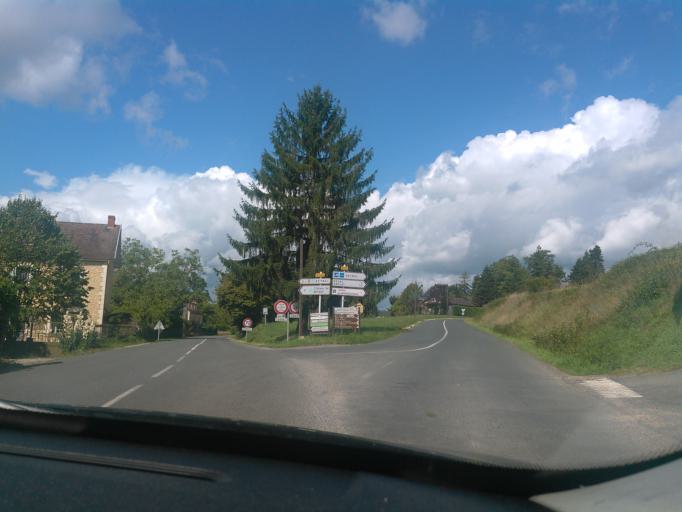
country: FR
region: Aquitaine
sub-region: Departement de la Dordogne
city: Cenac-et-Saint-Julien
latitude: 44.8235
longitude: 1.1570
